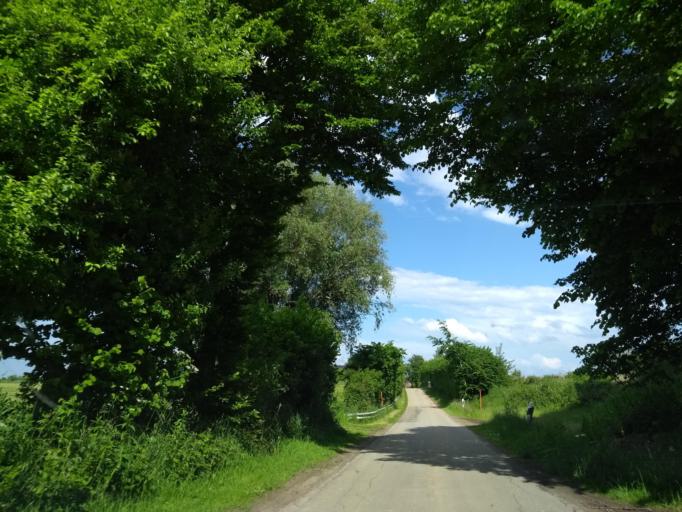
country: DE
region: Schleswig-Holstein
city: Thumby
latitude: 54.5540
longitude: 9.9363
